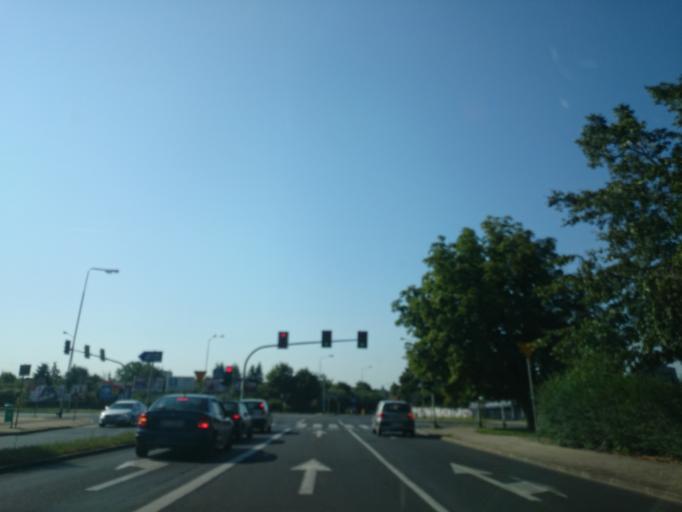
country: PL
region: West Pomeranian Voivodeship
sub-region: Szczecin
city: Szczecin
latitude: 53.4291
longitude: 14.5125
